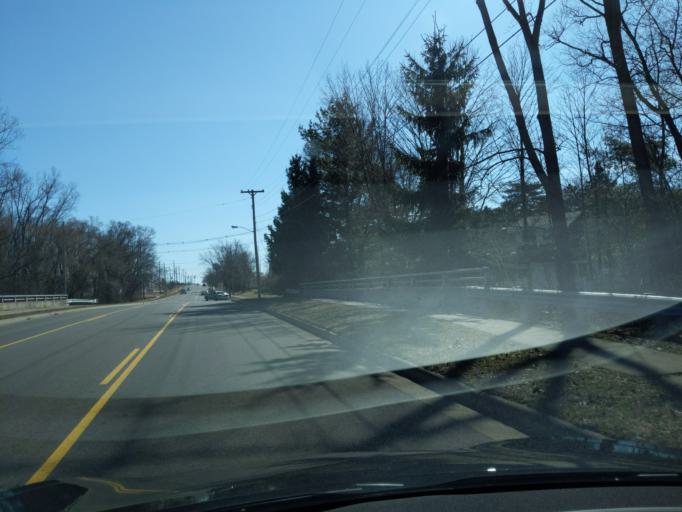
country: US
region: Michigan
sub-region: Ingham County
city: Mason
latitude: 42.5712
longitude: -84.4431
